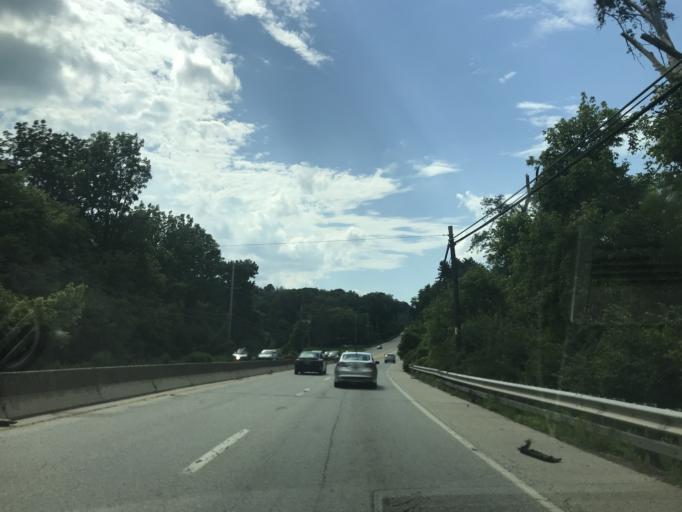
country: US
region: Pennsylvania
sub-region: Chester County
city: West Chester
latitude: 39.8715
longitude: -75.6057
